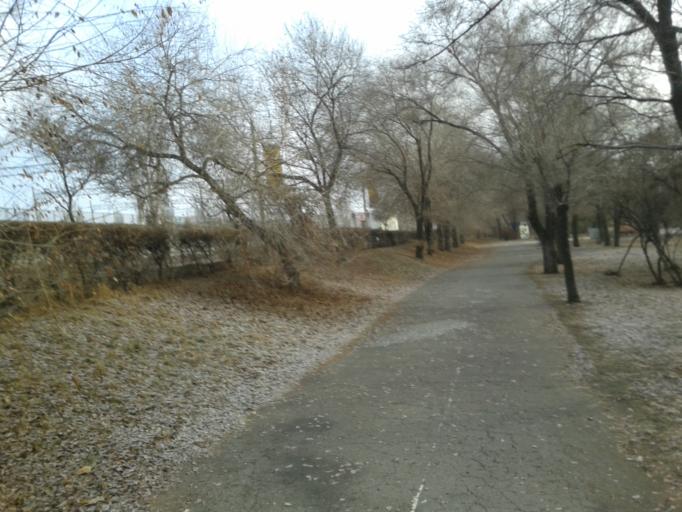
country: RU
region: Volgograd
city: Volgograd
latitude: 48.7098
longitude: 44.5056
